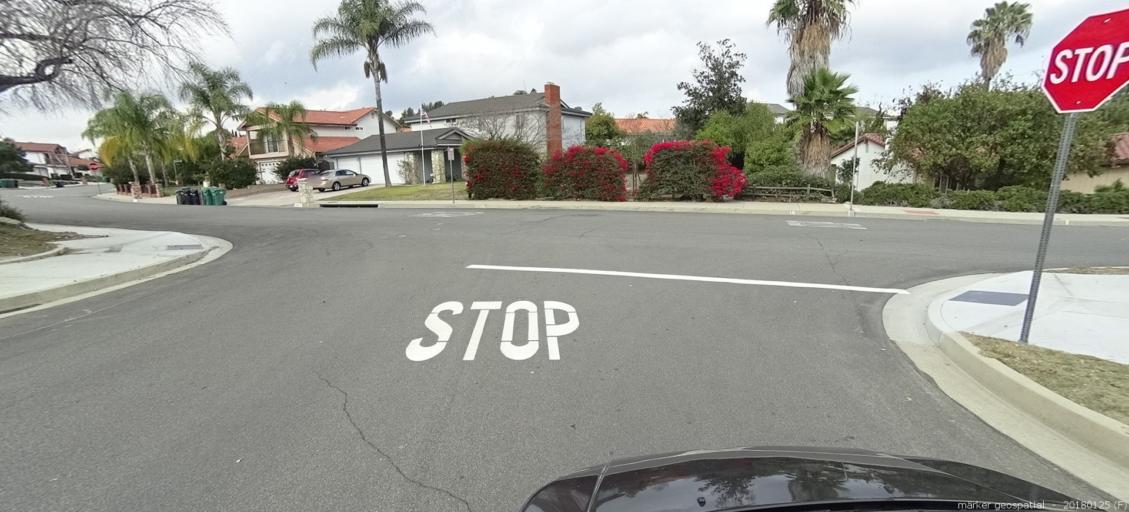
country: US
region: California
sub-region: Los Angeles County
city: Diamond Bar
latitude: 33.9896
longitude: -117.8314
